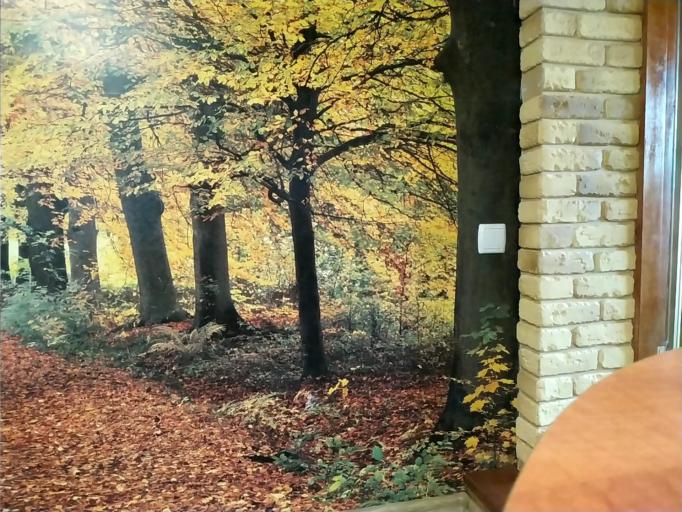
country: RU
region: Leningrad
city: Tolmachevo
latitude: 58.9353
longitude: 29.6973
